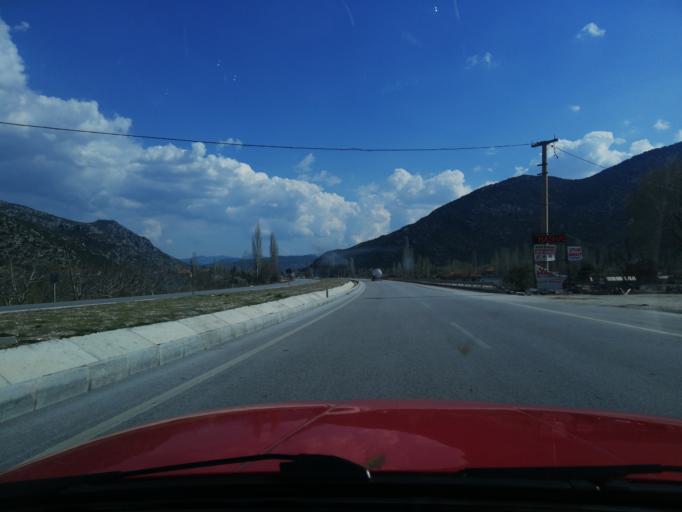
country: TR
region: Burdur
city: Celtikci
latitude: 37.5559
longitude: 30.4549
